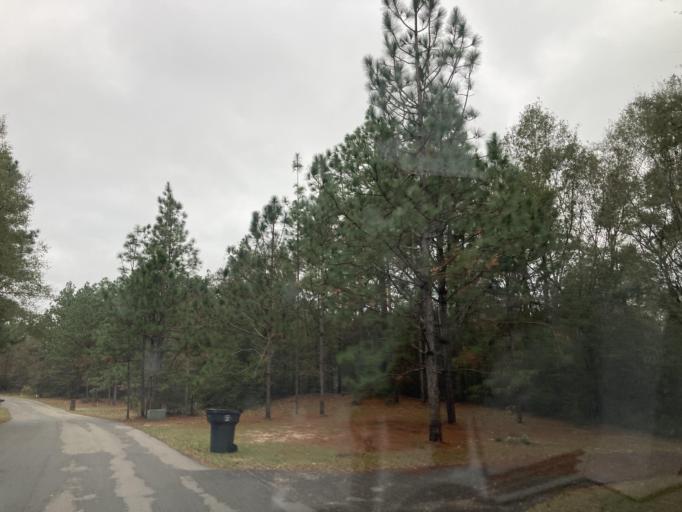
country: US
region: Mississippi
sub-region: Lamar County
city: Purvis
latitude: 31.1580
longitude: -89.4237
